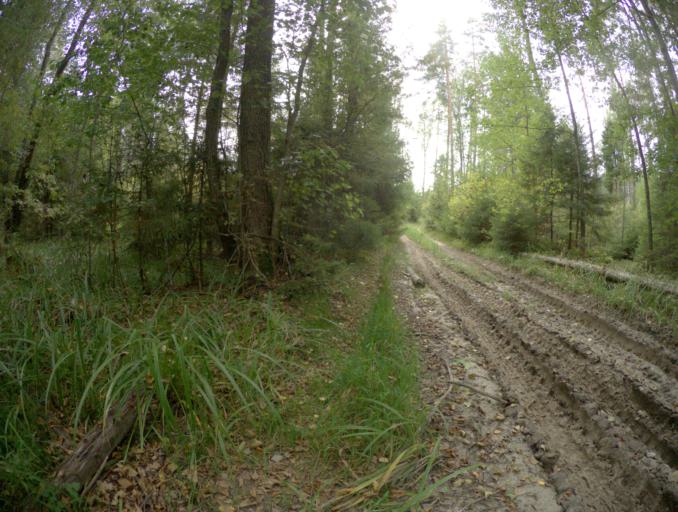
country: RU
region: Vladimir
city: Golovino
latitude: 55.9916
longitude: 40.4686
